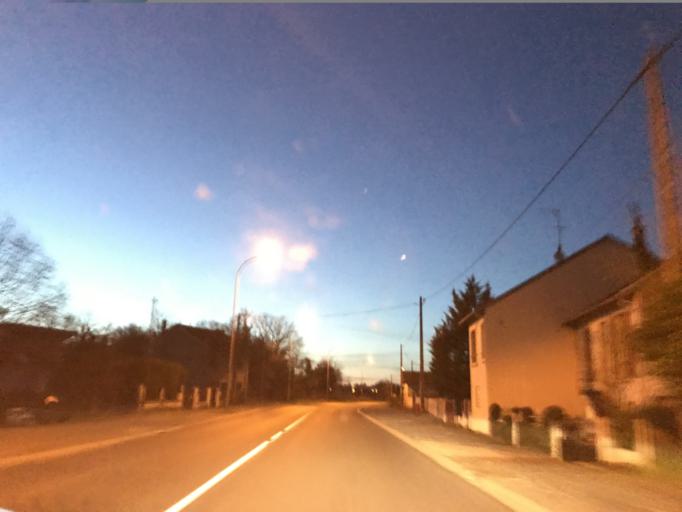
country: FR
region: Auvergne
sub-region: Departement de l'Allier
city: Vichy
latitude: 46.1051
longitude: 3.4235
